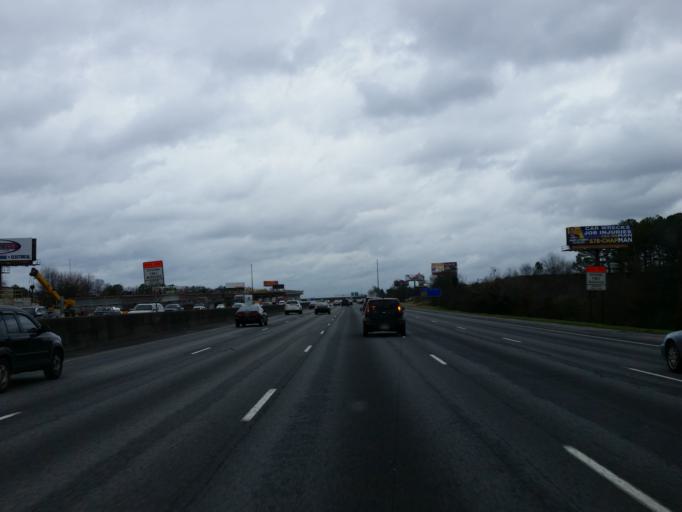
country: US
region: Georgia
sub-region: Cobb County
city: Marietta
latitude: 33.9739
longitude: -84.5315
